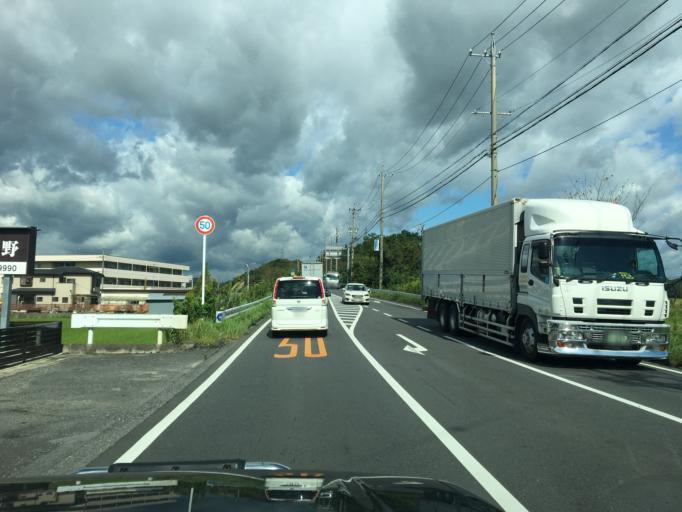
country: JP
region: Mie
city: Ueno-ebisumachi
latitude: 34.8108
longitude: 136.1852
